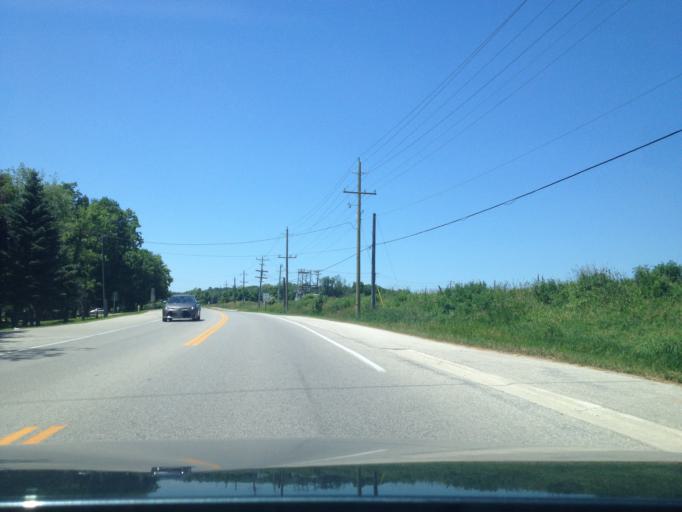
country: CA
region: Ontario
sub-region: Wellington County
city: Guelph
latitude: 43.6925
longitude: -80.4035
